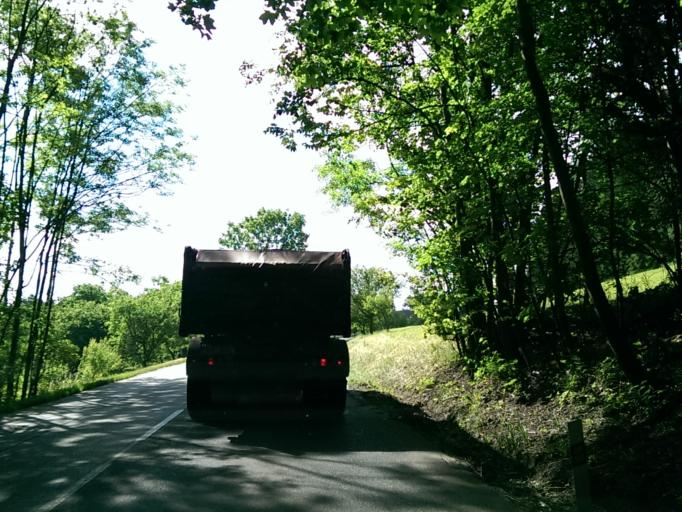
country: CZ
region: Liberecky
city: Rovensko pod Troskami
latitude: 50.5836
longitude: 15.2400
